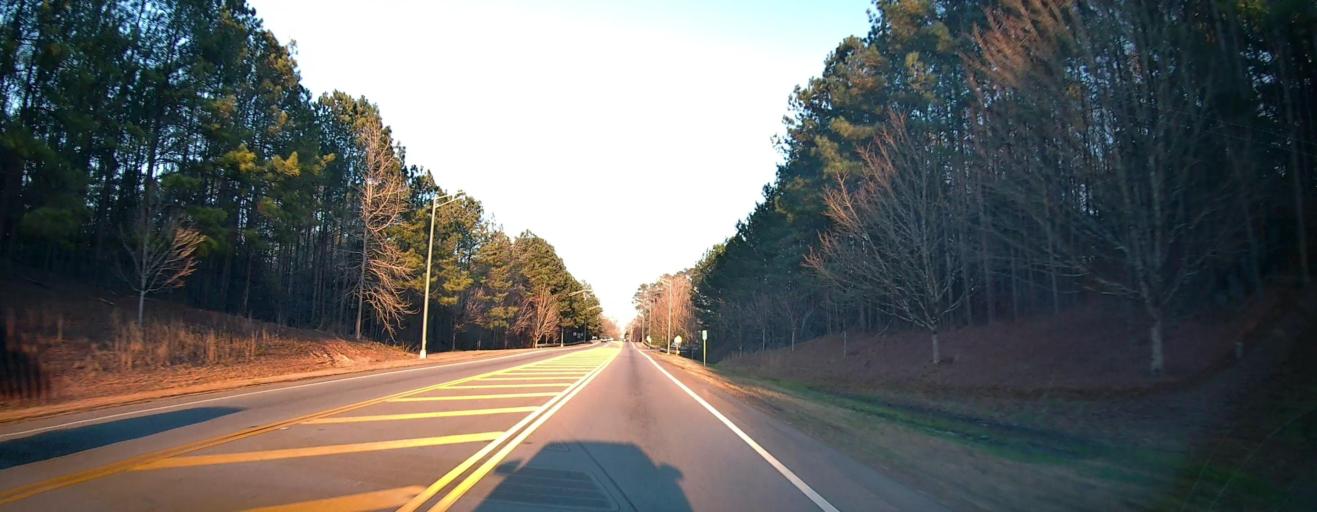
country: US
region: Georgia
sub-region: Troup County
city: La Grange
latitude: 33.0348
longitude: -85.0562
